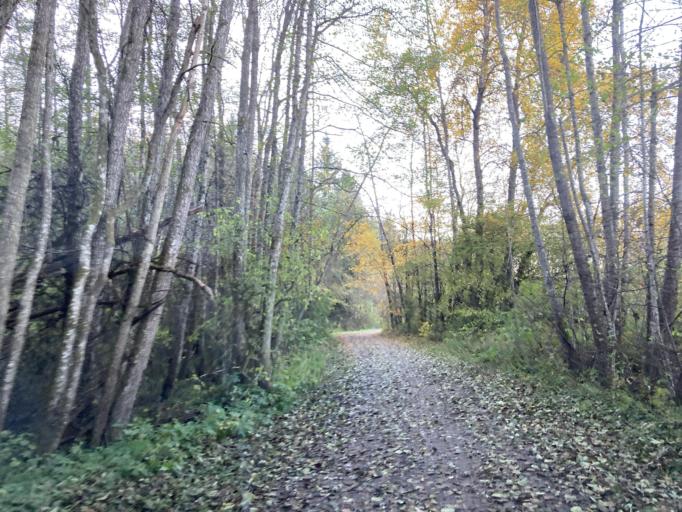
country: DE
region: Baden-Wuerttemberg
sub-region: Tuebingen Region
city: Bodelshausen
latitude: 48.4260
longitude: 8.9712
